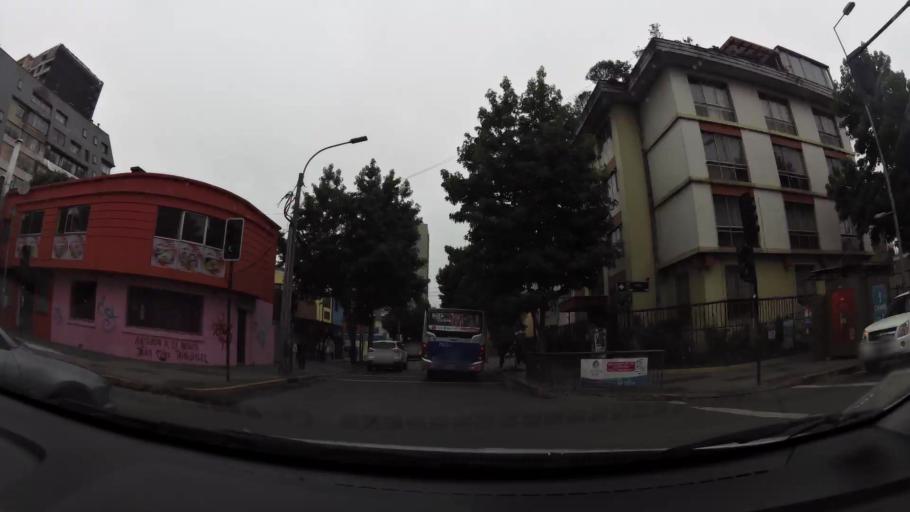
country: CL
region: Biobio
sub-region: Provincia de Concepcion
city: Concepcion
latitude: -36.8241
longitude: -73.0417
